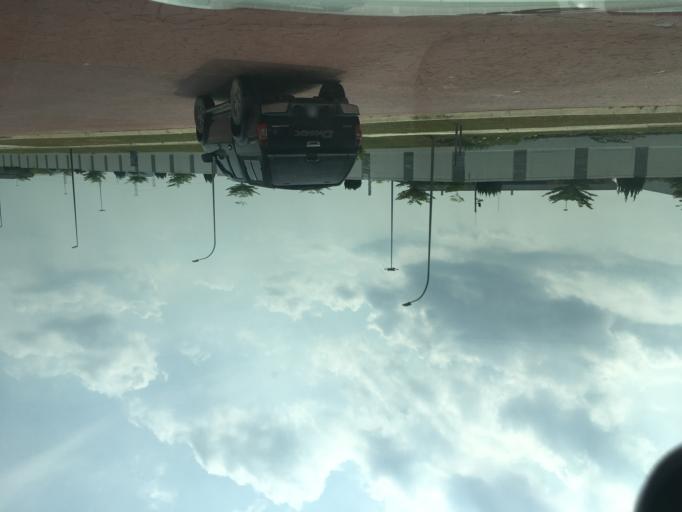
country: MY
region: Selangor
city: Klang
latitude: 3.0799
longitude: 101.4767
